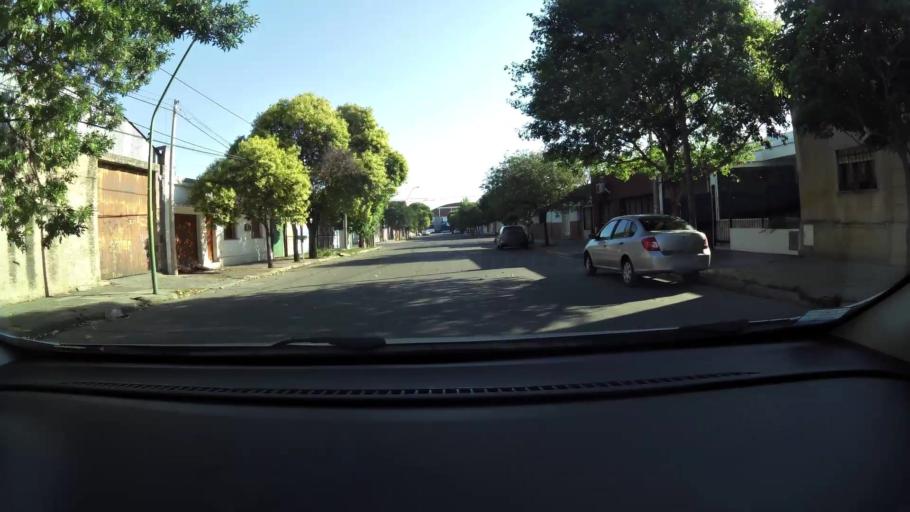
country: AR
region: Cordoba
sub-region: Departamento de Capital
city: Cordoba
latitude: -31.3954
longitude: -64.1770
